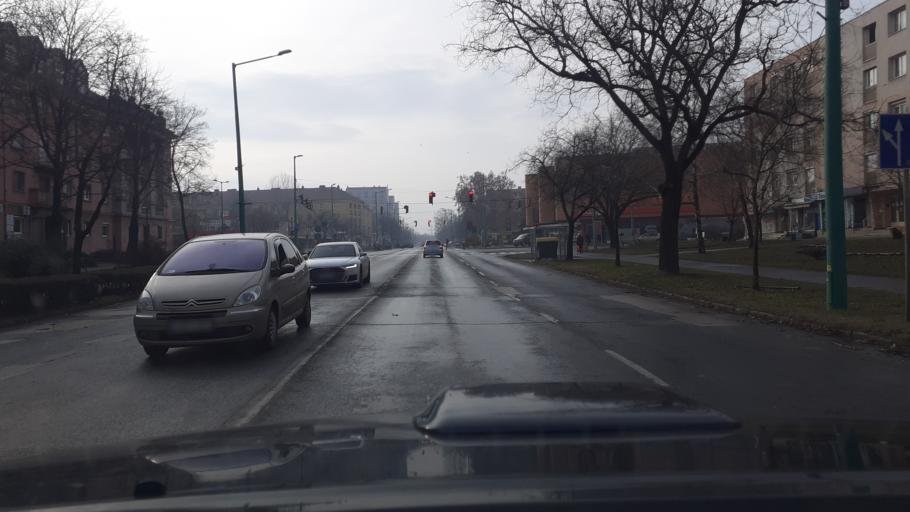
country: HU
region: Fejer
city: Dunaujvaros
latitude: 46.9630
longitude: 18.9355
